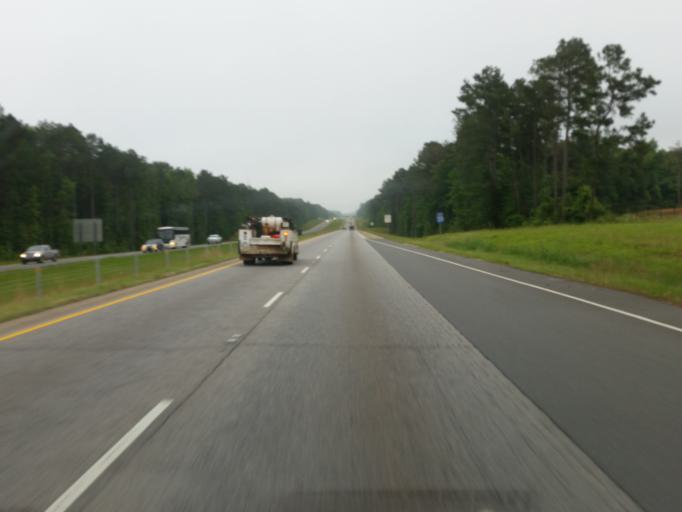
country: US
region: Louisiana
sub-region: Webster Parish
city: Minden
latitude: 32.5793
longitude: -93.2426
